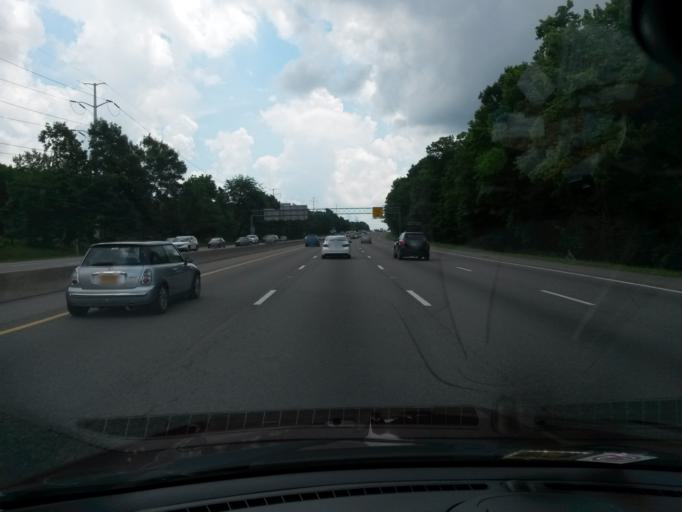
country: US
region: Virginia
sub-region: Chesterfield County
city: Bellwood
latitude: 37.4249
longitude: -77.4290
